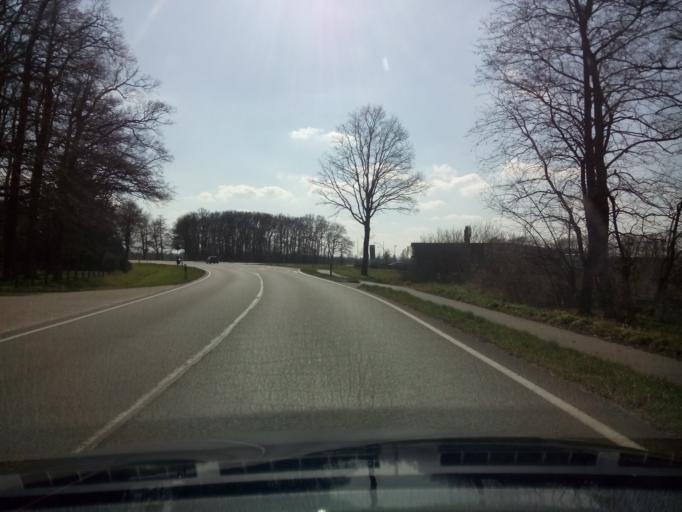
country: NL
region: Drenthe
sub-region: Gemeente Coevorden
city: Coevorden
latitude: 52.6433
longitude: 6.7570
